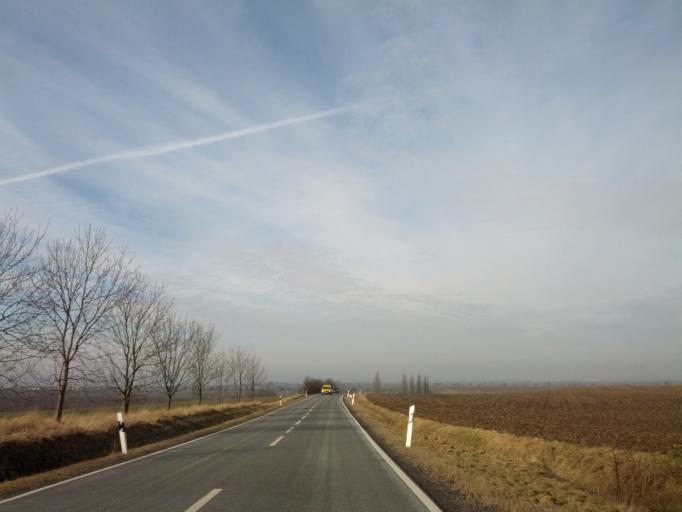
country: DE
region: Thuringia
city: Schonstedt
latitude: 51.1021
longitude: 10.5429
